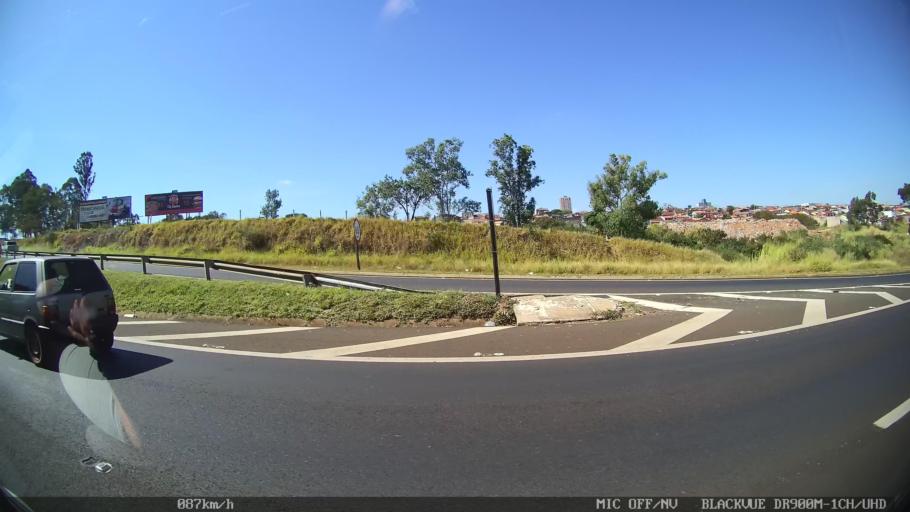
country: BR
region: Sao Paulo
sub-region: Franca
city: Franca
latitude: -20.5328
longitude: -47.4243
